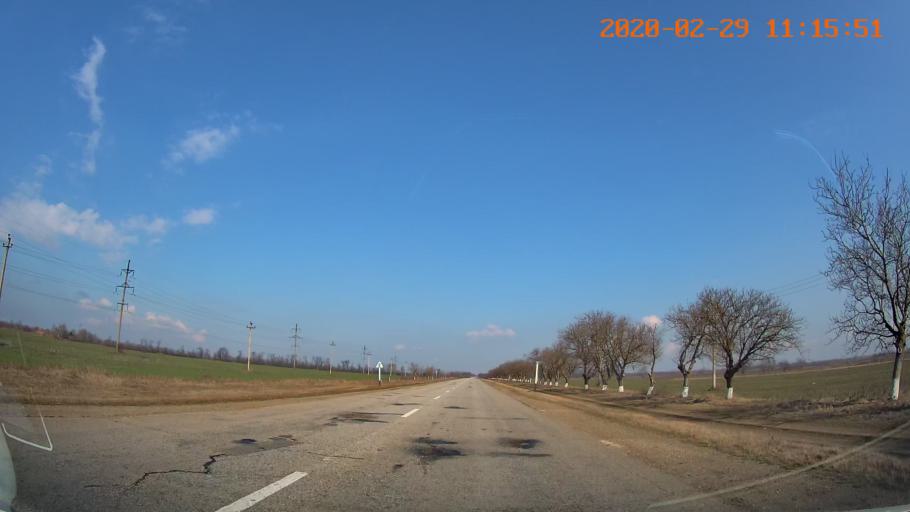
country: MD
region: Telenesti
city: Dubasari
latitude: 47.3004
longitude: 29.1662
